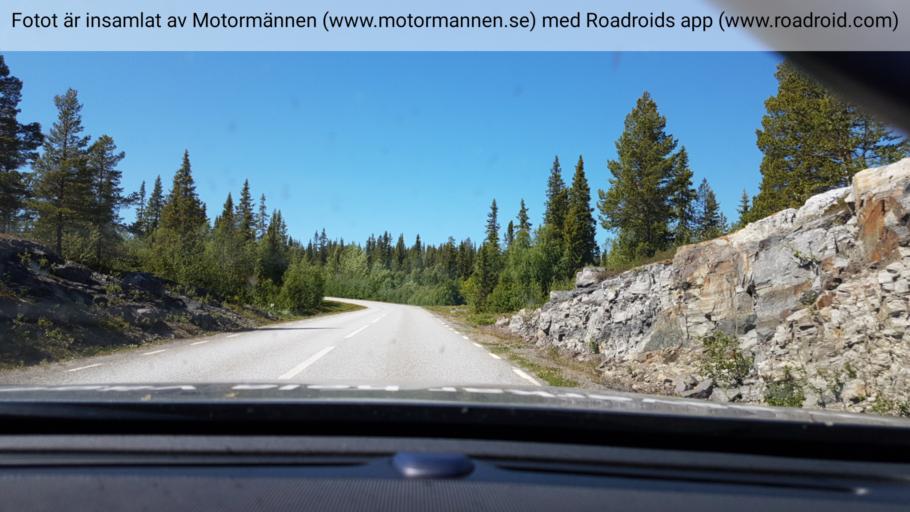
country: SE
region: Vaesterbotten
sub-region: Vilhelmina Kommun
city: Sjoberg
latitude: 64.9569
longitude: 15.4601
